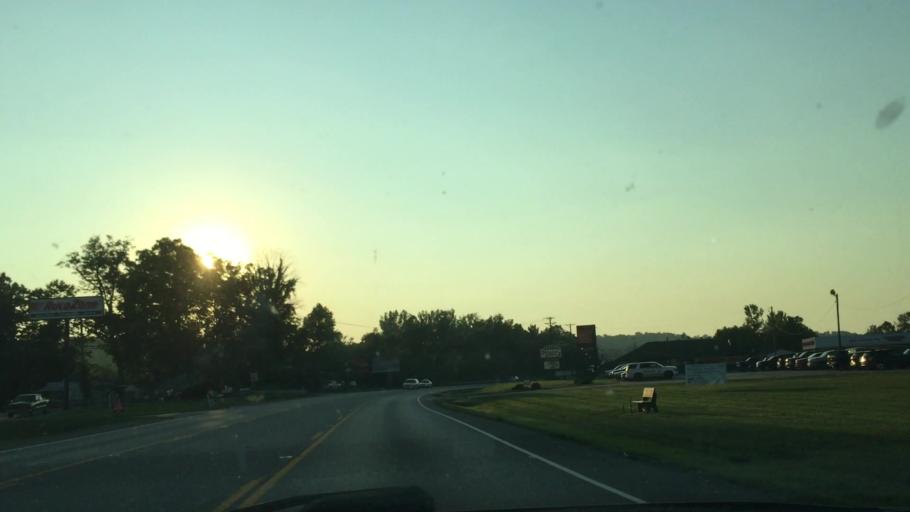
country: US
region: Kentucky
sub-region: Carroll County
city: Carrollton
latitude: 38.6578
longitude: -85.1351
